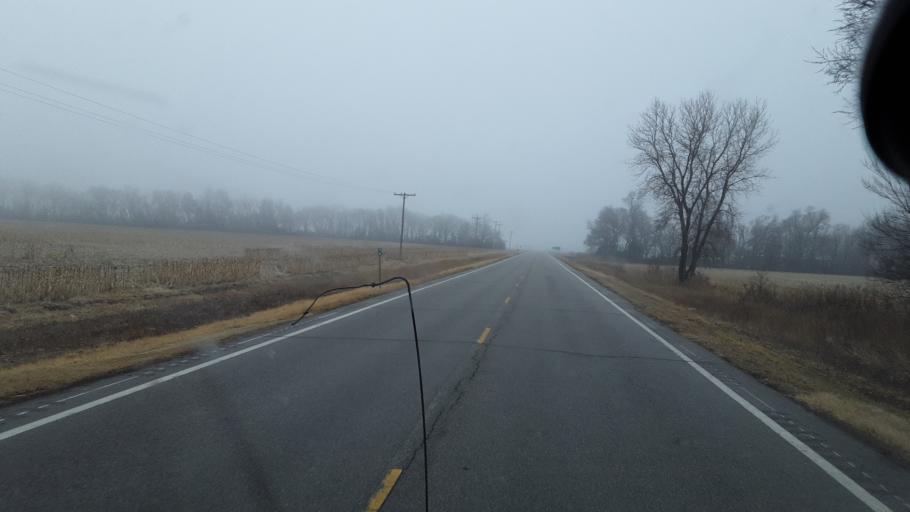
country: US
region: Kansas
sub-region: Reno County
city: South Hutchinson
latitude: 37.9447
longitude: -97.9405
